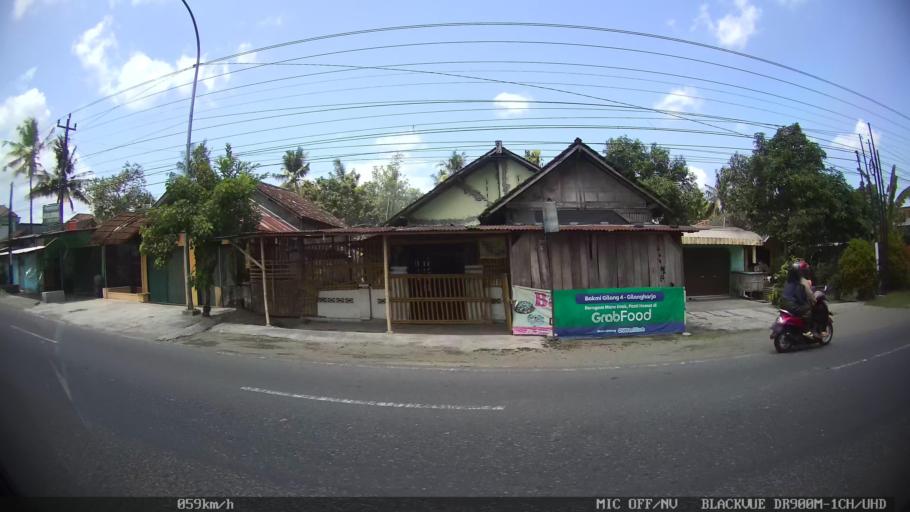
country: ID
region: Daerah Istimewa Yogyakarta
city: Pandak
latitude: -7.9075
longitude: 110.3043
